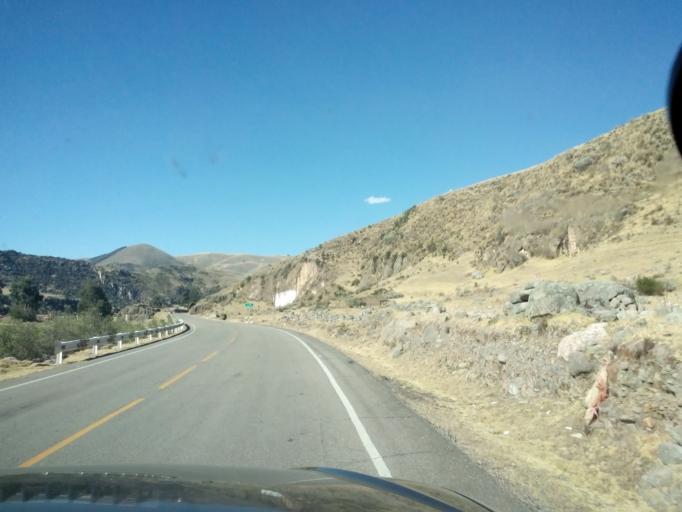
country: PE
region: Ayacucho
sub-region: Provincia de Huamanga
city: Vinchos
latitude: -13.3395
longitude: -74.3726
